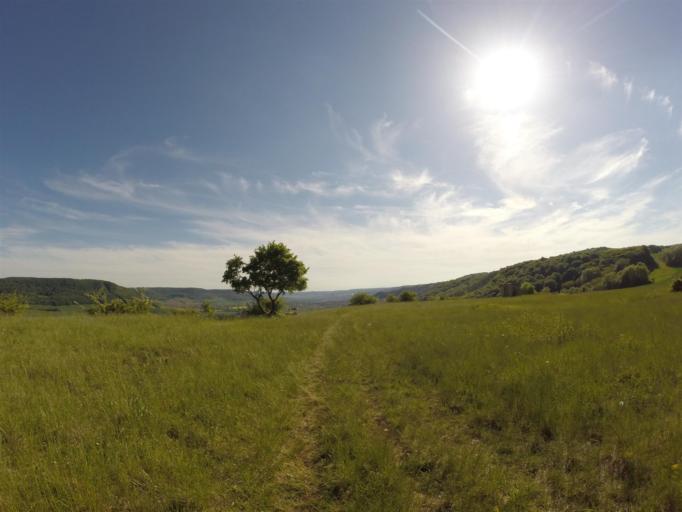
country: DE
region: Thuringia
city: Neuengonna
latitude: 50.9811
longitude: 11.6456
